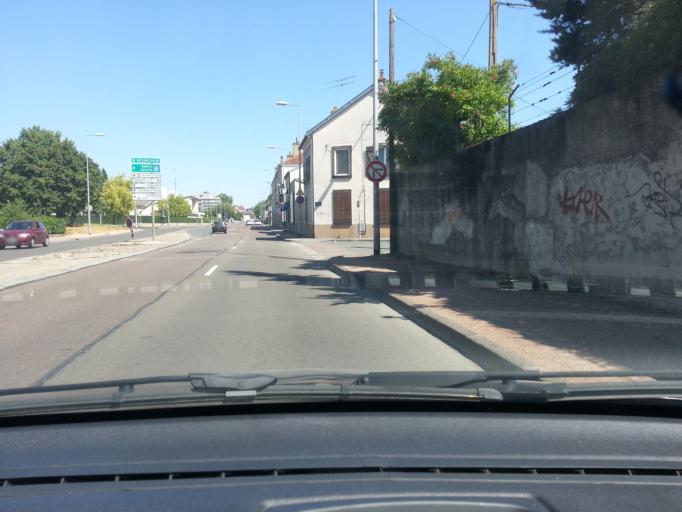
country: FR
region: Bourgogne
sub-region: Departement de la Cote-d'Or
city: Dijon
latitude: 47.3085
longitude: 5.0318
